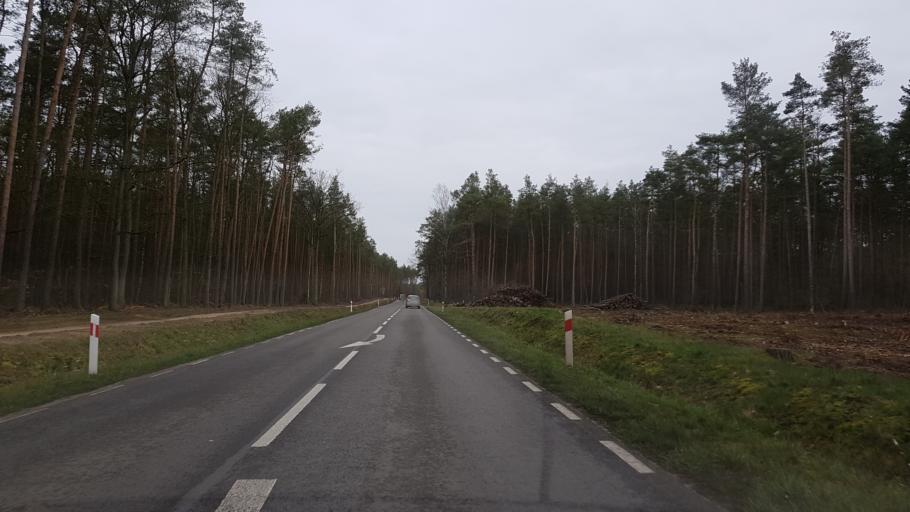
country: PL
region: West Pomeranian Voivodeship
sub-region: Powiat policki
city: Police
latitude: 53.6309
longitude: 14.5029
